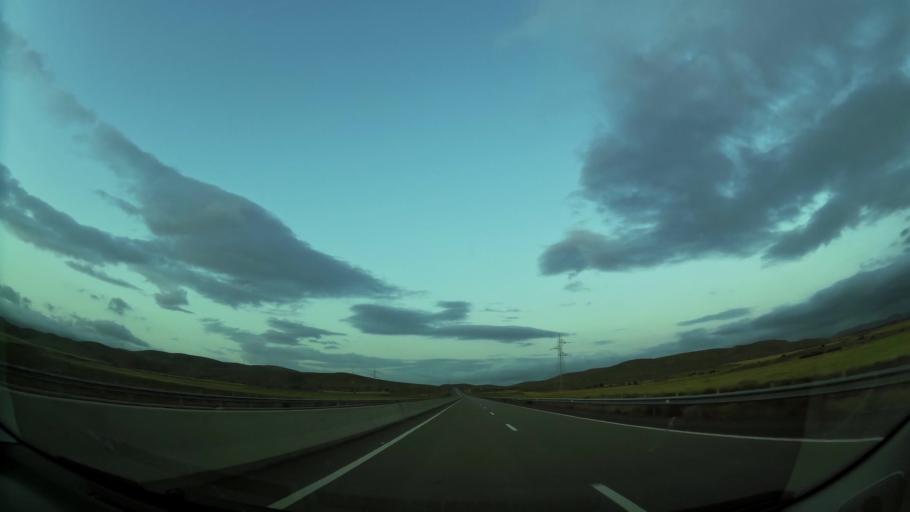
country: MA
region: Oriental
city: El Aioun
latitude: 34.6049
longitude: -2.6071
